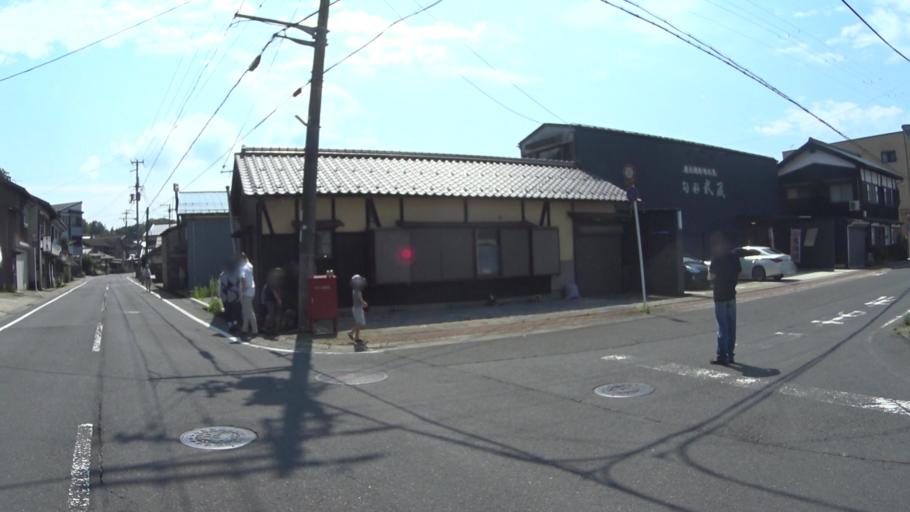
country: JP
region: Kyoto
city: Miyazu
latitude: 35.6231
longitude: 135.0615
